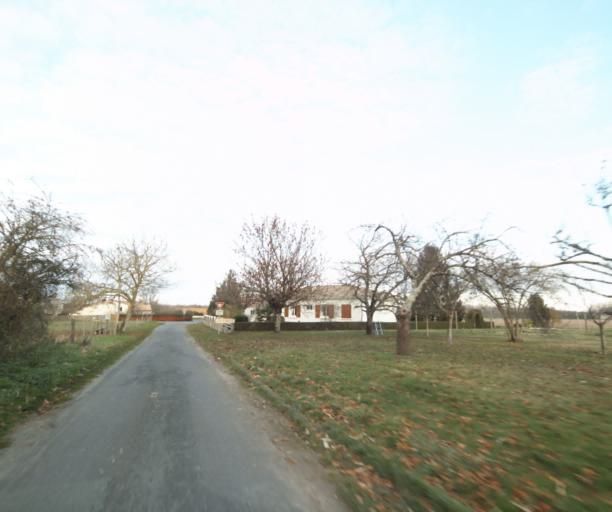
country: FR
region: Poitou-Charentes
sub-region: Departement de la Charente-Maritime
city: Les Gonds
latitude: 45.7090
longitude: -0.6116
